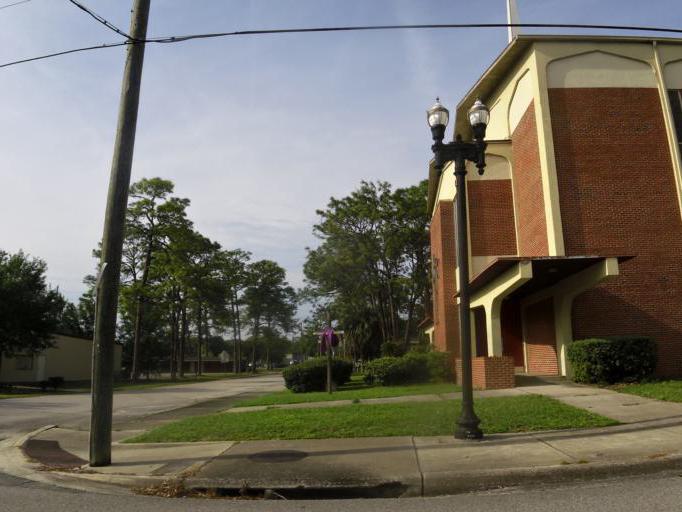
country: US
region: Florida
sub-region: Duval County
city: Jacksonville
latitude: 30.3337
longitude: -81.5922
